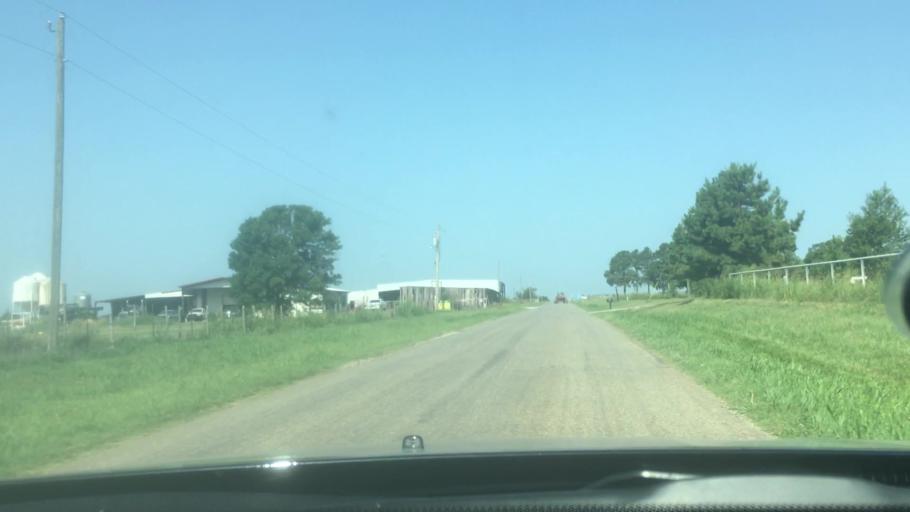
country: US
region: Oklahoma
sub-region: Bryan County
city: Calera
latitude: 33.9400
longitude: -96.4520
